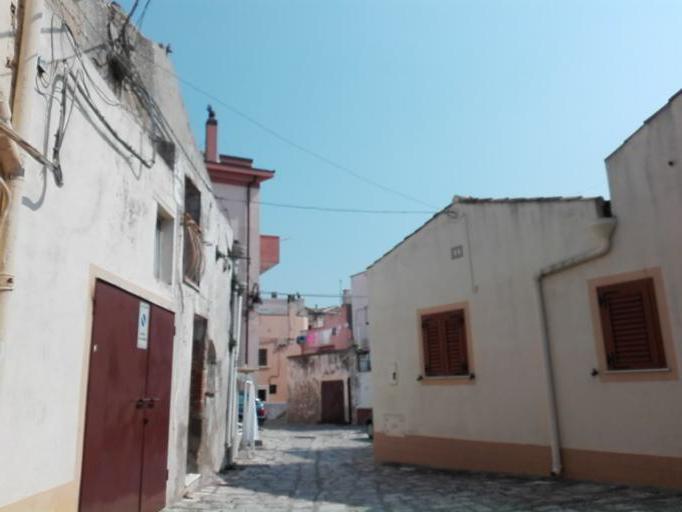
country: IT
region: Basilicate
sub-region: Provincia di Matera
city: Miglionico
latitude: 40.5706
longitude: 16.4999
